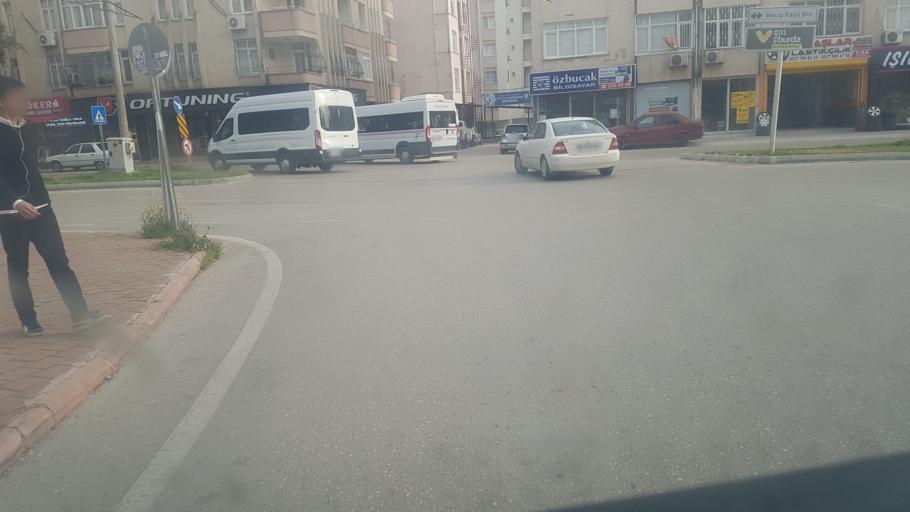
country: TR
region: Adana
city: Adana
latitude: 37.0268
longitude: 35.3107
